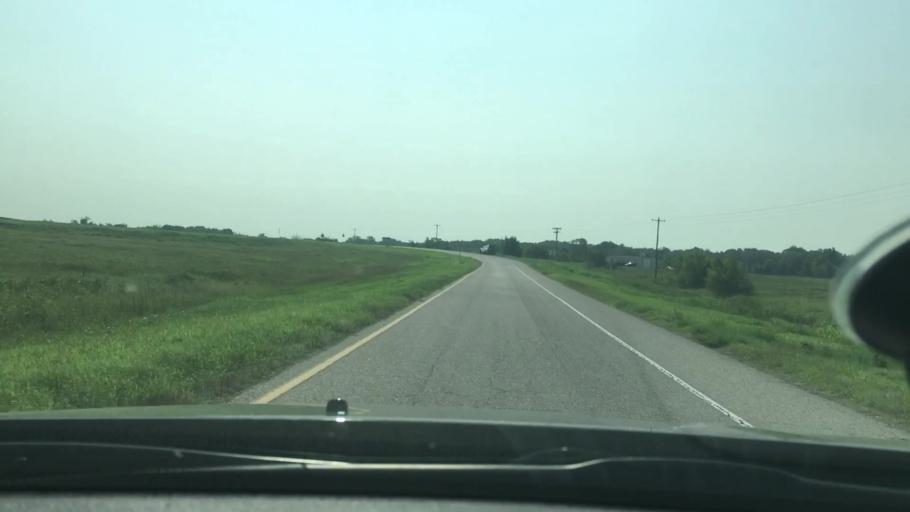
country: US
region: Oklahoma
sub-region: Pontotoc County
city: Ada
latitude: 34.6415
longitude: -96.5328
